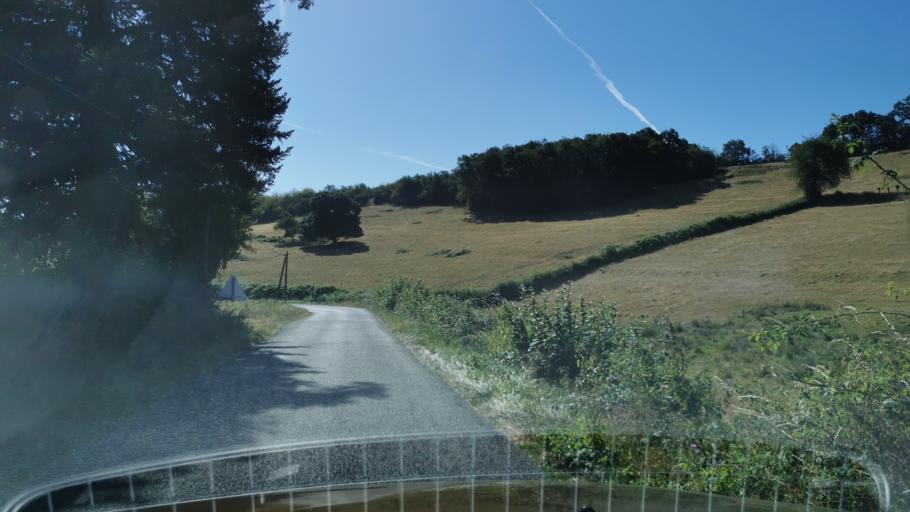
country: FR
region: Bourgogne
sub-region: Departement de Saone-et-Loire
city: Marmagne
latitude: 46.8056
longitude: 4.3142
